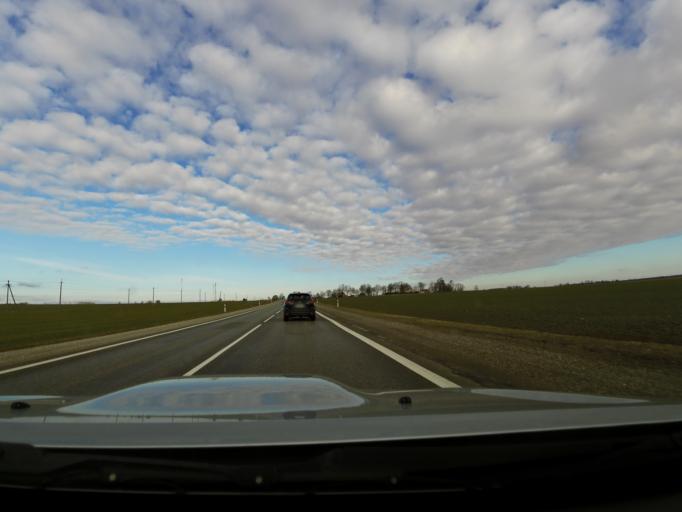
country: LT
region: Siauliu apskritis
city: Pakruojis
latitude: 55.7845
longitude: 24.0405
